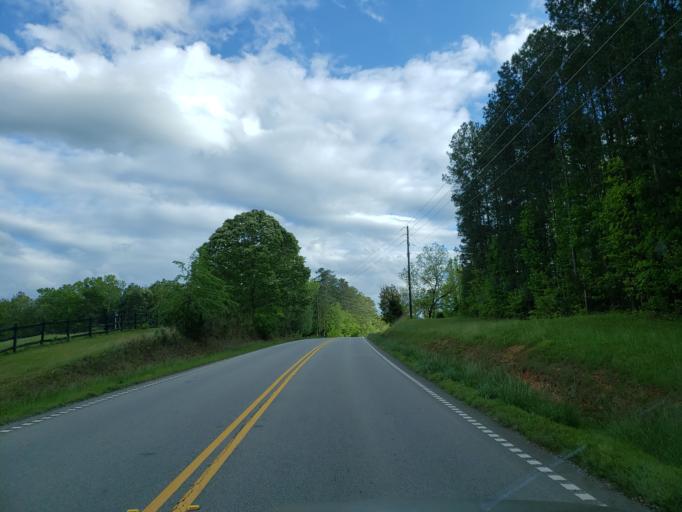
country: US
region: Georgia
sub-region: Haralson County
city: Tallapoosa
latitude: 33.8242
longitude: -85.2915
